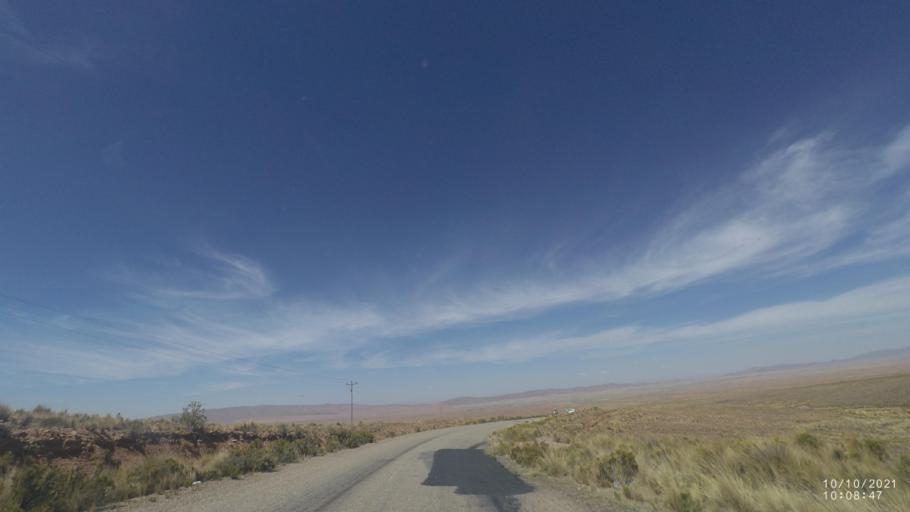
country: BO
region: La Paz
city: Eucaliptus
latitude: -17.3946
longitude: -67.4806
